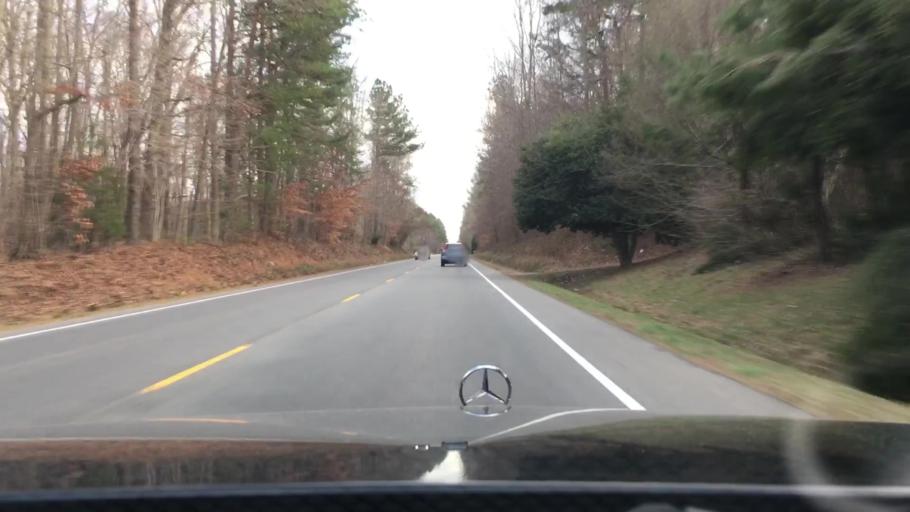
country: US
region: North Carolina
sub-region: Orange County
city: Hillsborough
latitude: 36.0624
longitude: -79.0562
